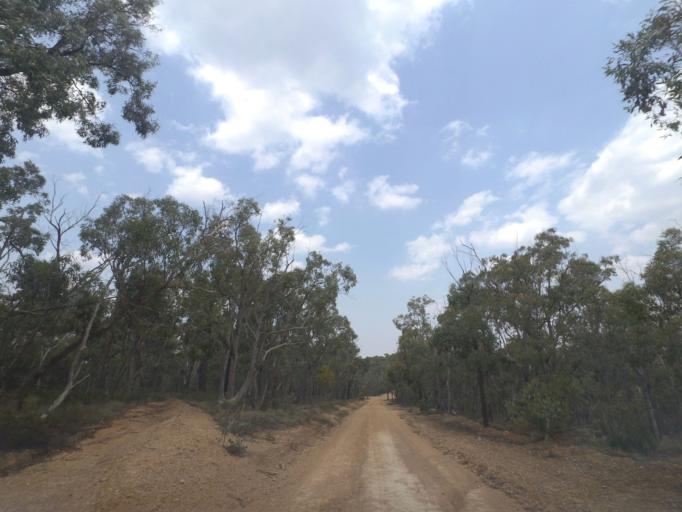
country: AU
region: Victoria
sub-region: Moorabool
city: Bacchus Marsh
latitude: -37.5815
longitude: 144.4410
